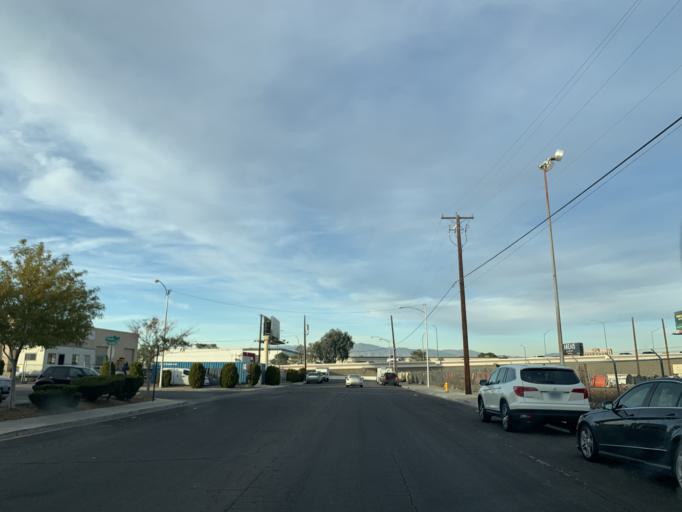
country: US
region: Nevada
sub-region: Clark County
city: Paradise
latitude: 36.1279
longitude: -115.1833
